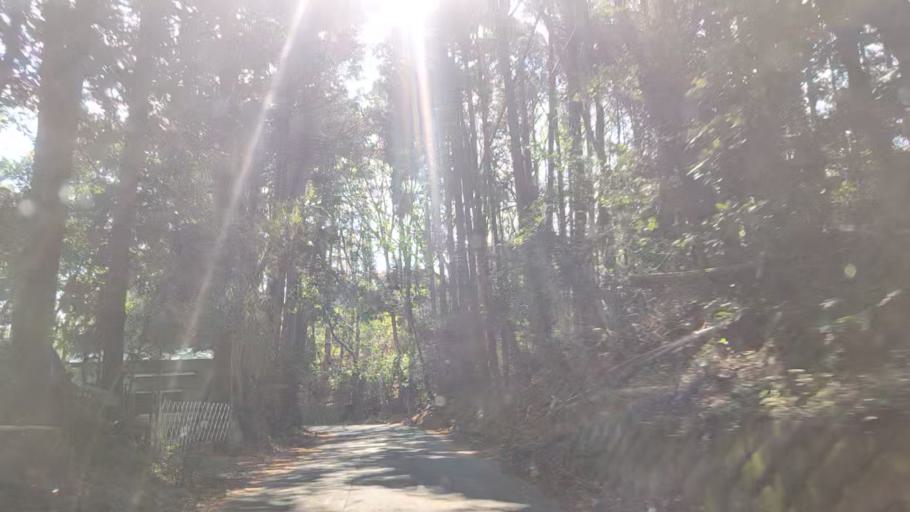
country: JP
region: Kanagawa
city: Ninomiya
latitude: 35.3264
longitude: 139.2625
